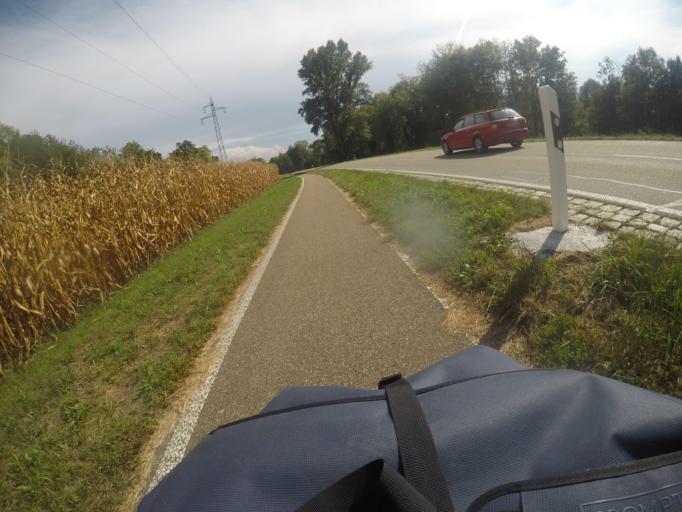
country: FR
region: Alsace
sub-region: Departement du Haut-Rhin
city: Rosenau
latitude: 47.6632
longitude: 7.5277
